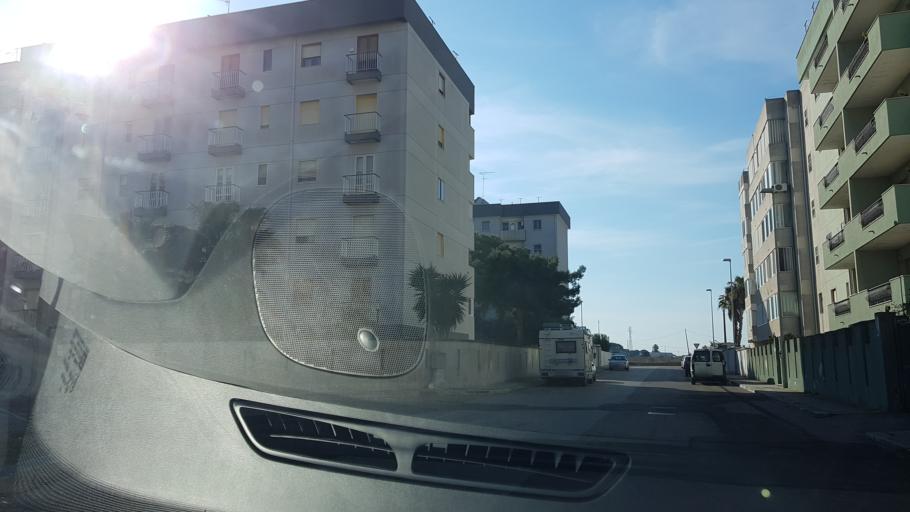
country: IT
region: Apulia
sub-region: Provincia di Brindisi
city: Brindisi
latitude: 40.6179
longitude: 17.9189
